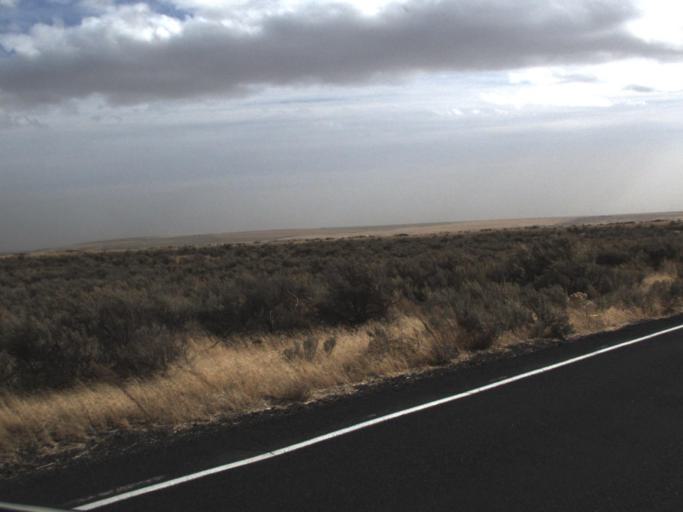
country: US
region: Washington
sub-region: Okanogan County
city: Coulee Dam
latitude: 47.5641
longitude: -118.7859
